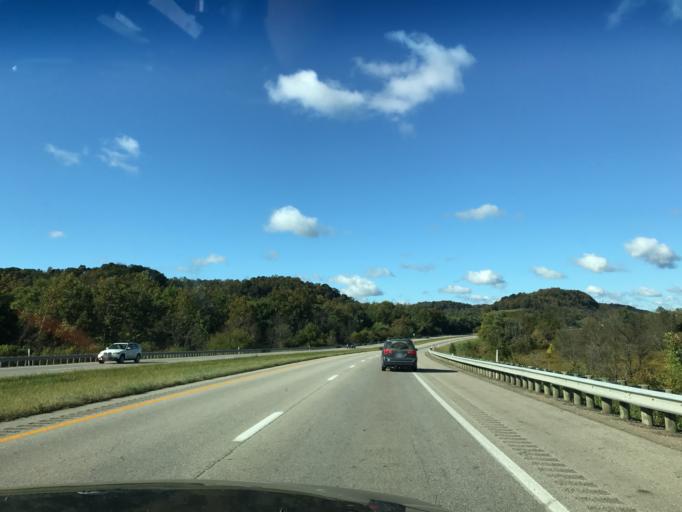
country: US
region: Ohio
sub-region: Athens County
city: Athens
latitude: 39.3326
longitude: -82.0379
